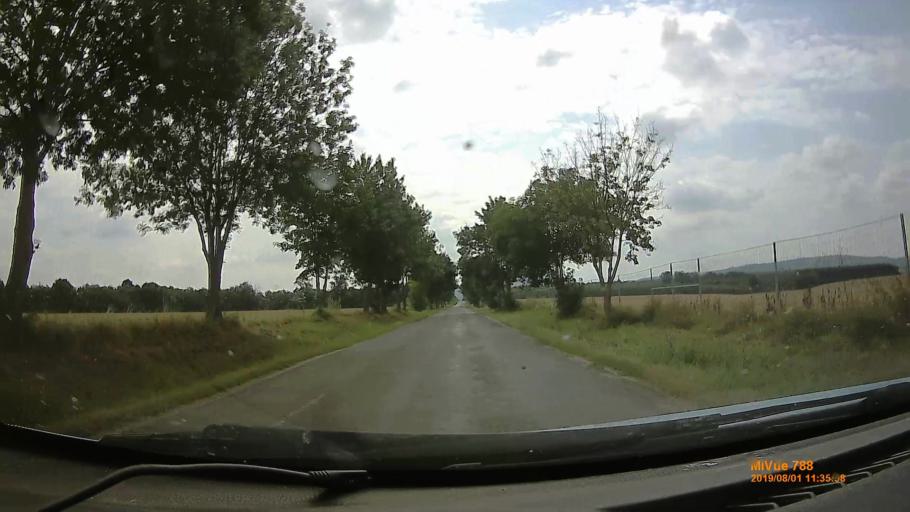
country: HU
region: Baranya
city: Villany
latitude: 45.9220
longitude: 18.3718
